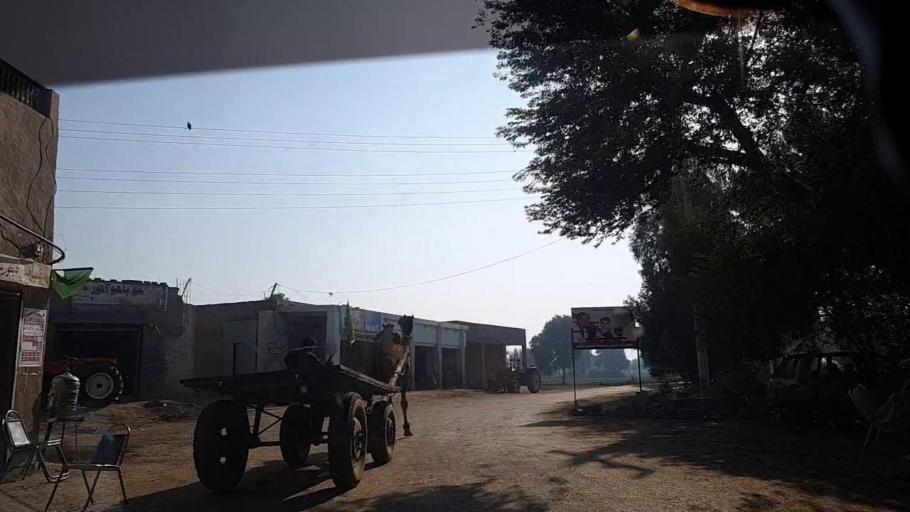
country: PK
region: Sindh
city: Sobhadero
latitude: 27.2515
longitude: 68.2976
